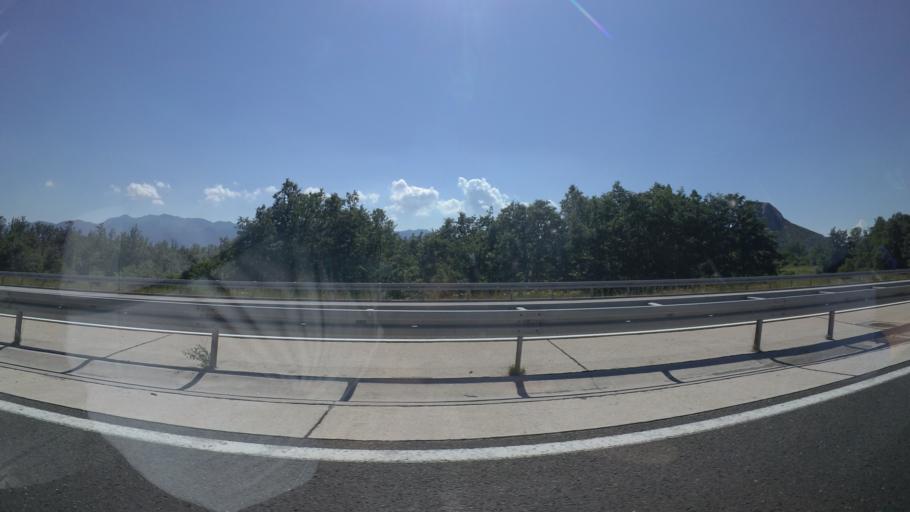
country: HR
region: Zadarska
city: Obrovac
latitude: 44.4250
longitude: 15.6351
